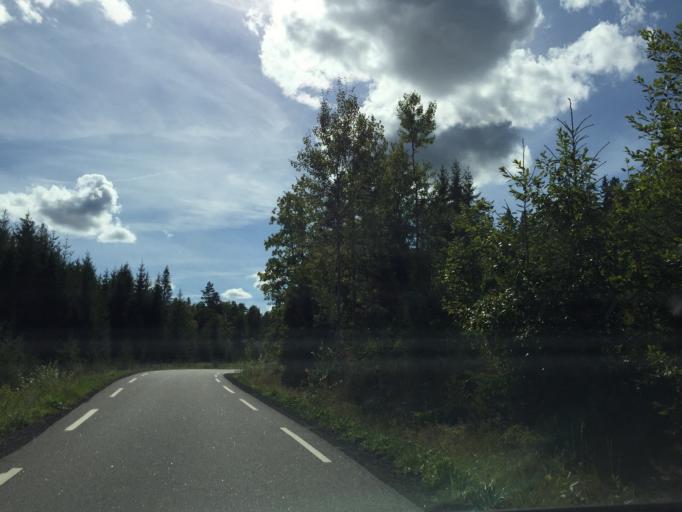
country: NO
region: Vestfold
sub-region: Holmestrand
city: Gullhaug
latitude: 59.4358
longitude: 10.1598
